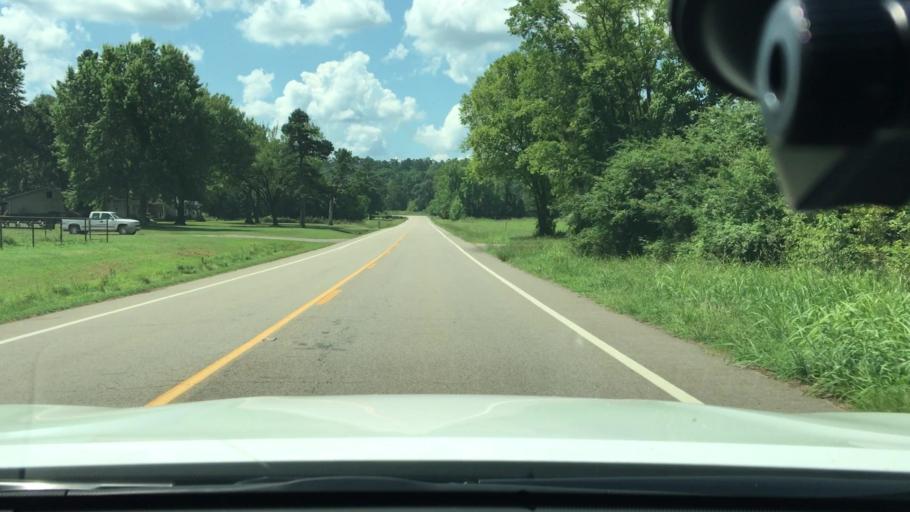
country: US
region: Arkansas
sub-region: Logan County
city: Paris
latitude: 35.2616
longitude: -93.6833
